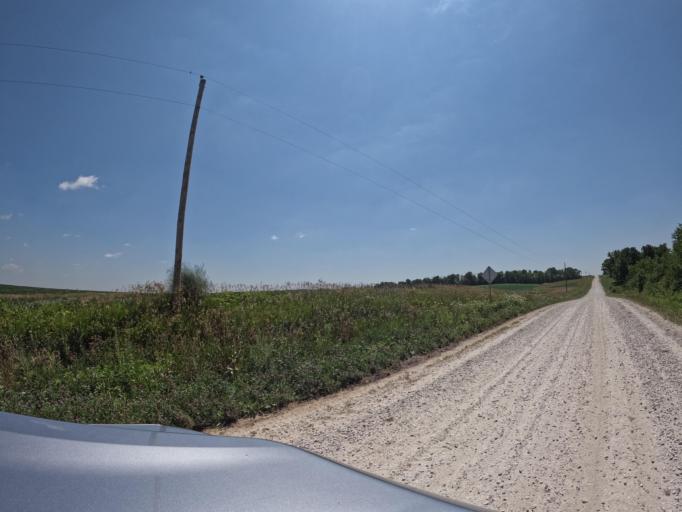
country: US
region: Iowa
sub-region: Keokuk County
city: Sigourney
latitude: 41.2860
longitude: -92.2382
